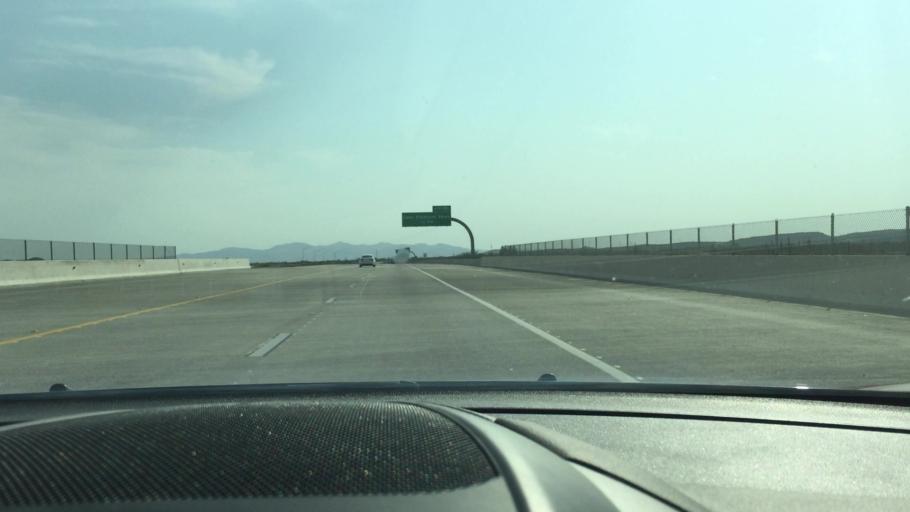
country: US
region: Arizona
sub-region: Maricopa County
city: Anthem
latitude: 33.7766
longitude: -112.2368
